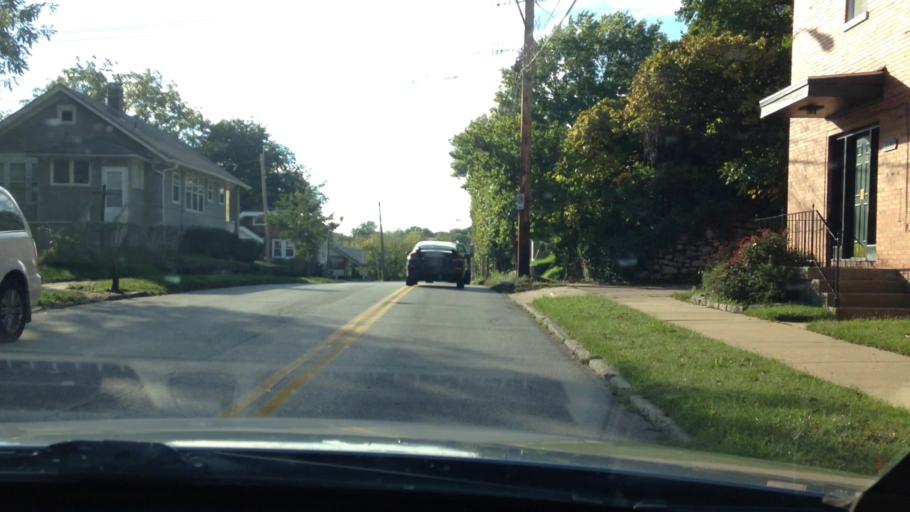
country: US
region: Kansas
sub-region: Johnson County
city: Westwood
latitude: 39.0427
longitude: -94.6037
